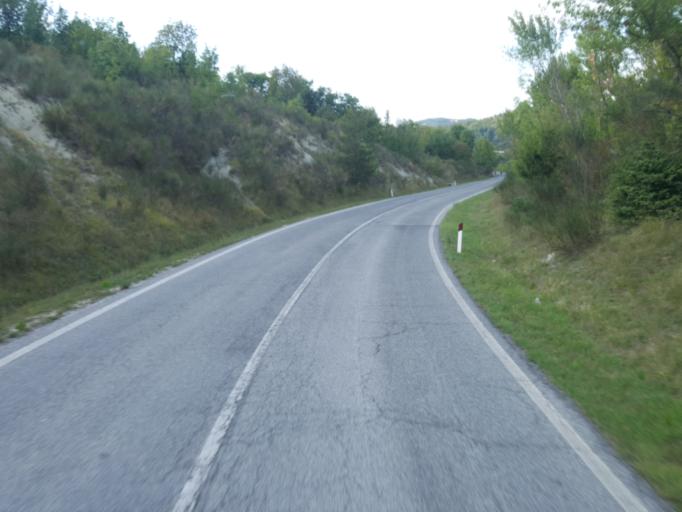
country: IT
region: Umbria
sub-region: Provincia di Perugia
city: Fossato di Vico
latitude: 43.3286
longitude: 12.8306
